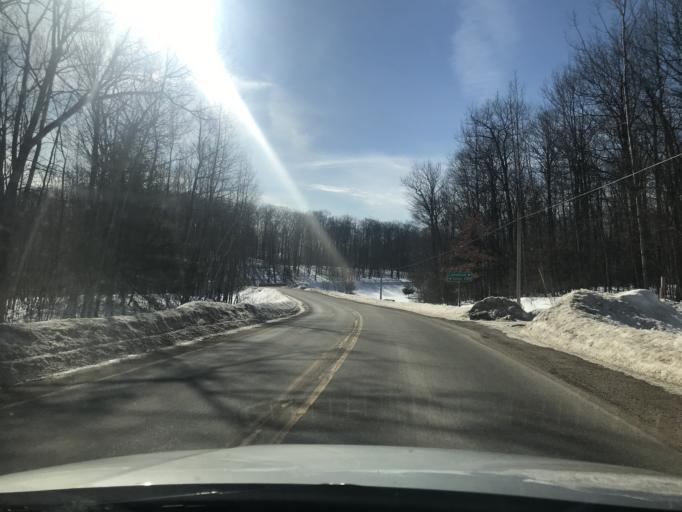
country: US
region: Michigan
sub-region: Dickinson County
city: Kingsford
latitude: 45.3977
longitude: -88.3418
